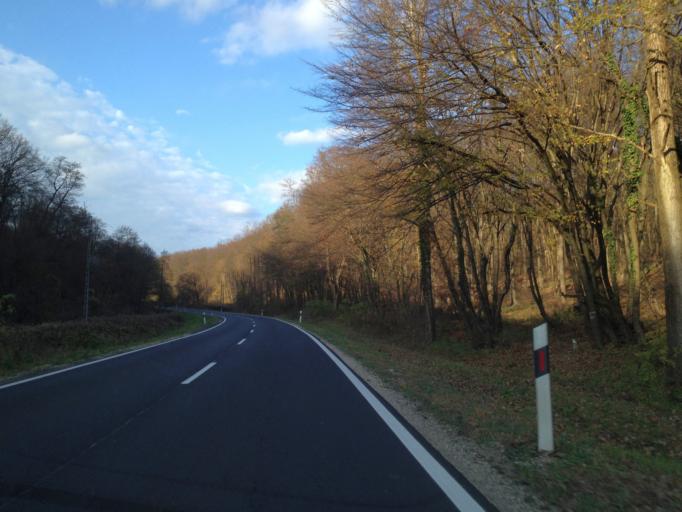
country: HU
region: Gyor-Moson-Sopron
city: Bakonyszentlaszlo
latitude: 47.4036
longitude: 17.8549
